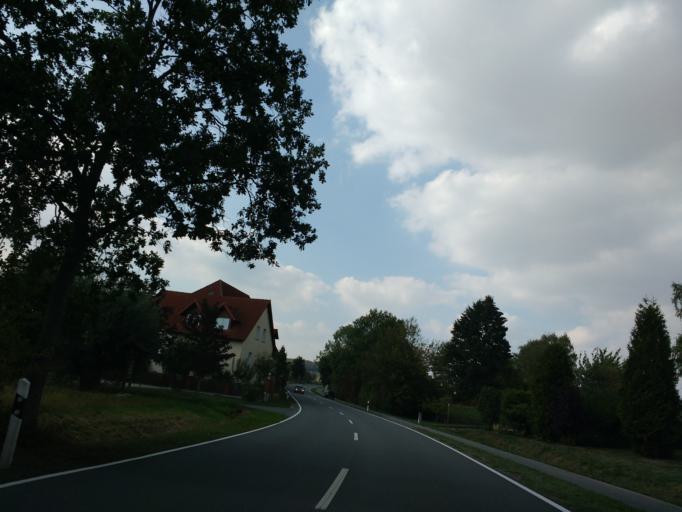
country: DE
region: North Rhine-Westphalia
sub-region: Regierungsbezirk Detmold
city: Bad Meinberg
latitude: 51.9339
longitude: 9.0263
